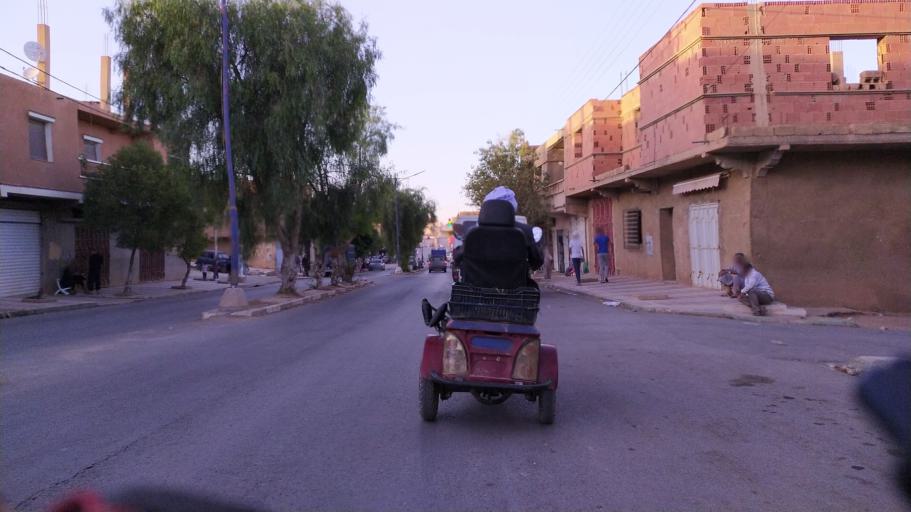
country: DZ
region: Tiaret
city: Frenda
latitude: 34.8932
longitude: 1.2467
